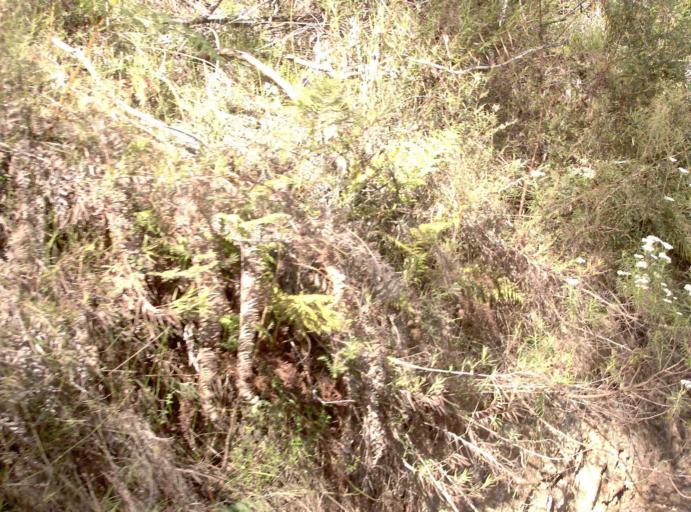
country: AU
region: Victoria
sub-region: East Gippsland
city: Lakes Entrance
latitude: -37.4132
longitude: 148.5994
